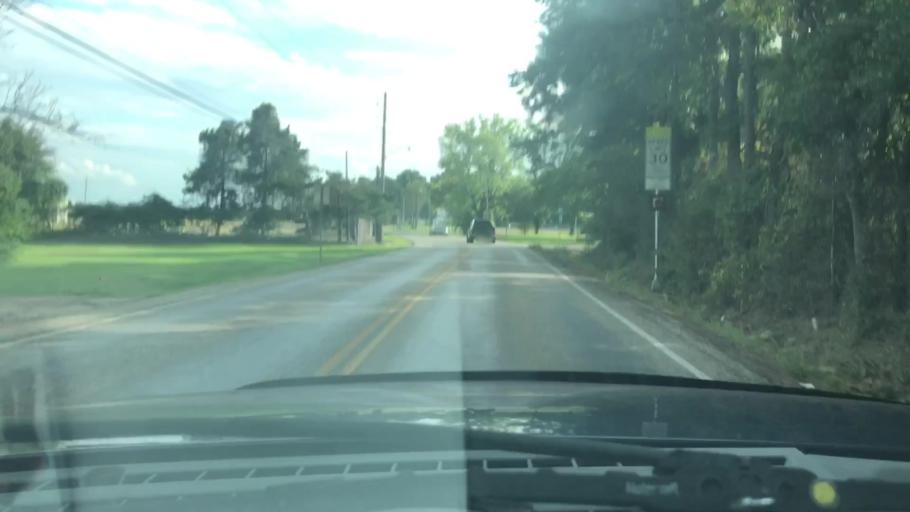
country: US
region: Texas
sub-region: Bowie County
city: Texarkana
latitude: 33.3973
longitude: -94.0642
